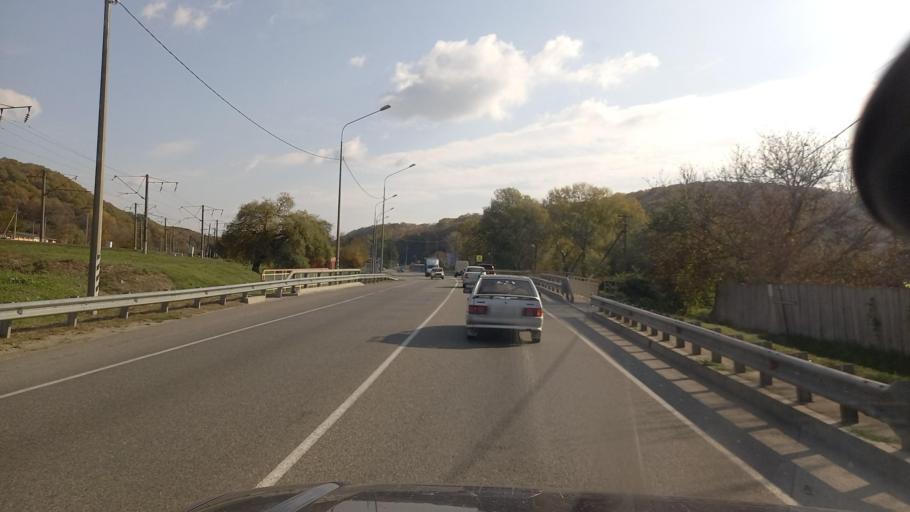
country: RU
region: Krasnodarskiy
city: Krymsk
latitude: 44.8690
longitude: 37.8846
